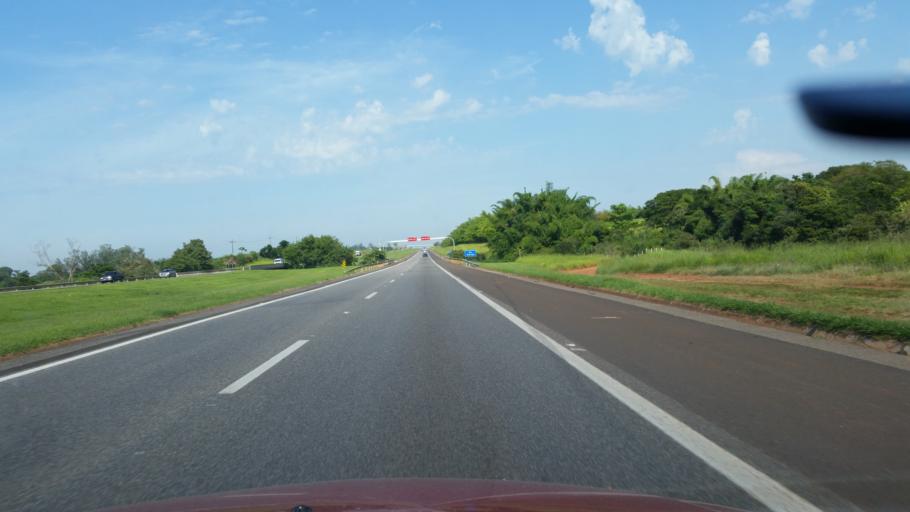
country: BR
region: Sao Paulo
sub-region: Tatui
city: Tatui
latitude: -23.2583
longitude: -47.8698
